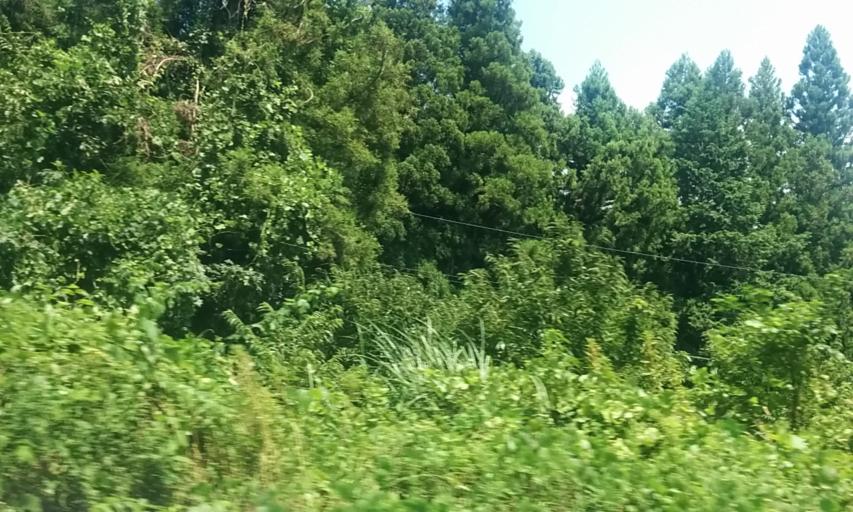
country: JP
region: Kyoto
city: Fukuchiyama
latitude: 35.2554
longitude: 135.1480
